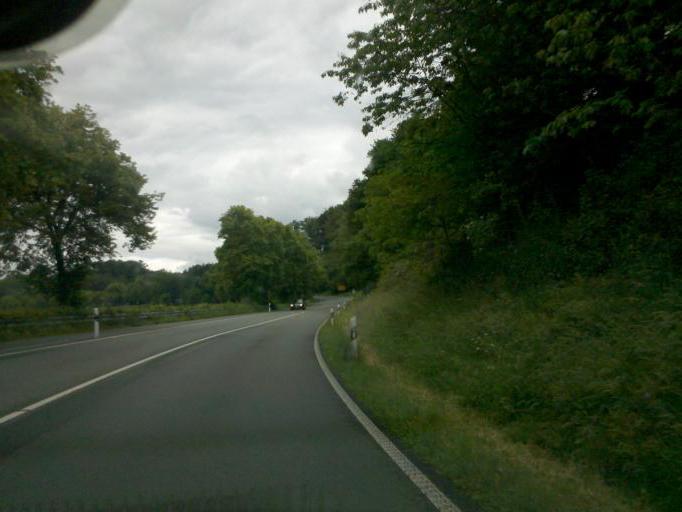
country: DE
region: North Rhine-Westphalia
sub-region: Regierungsbezirk Arnsberg
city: Meschede
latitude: 51.3050
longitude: 8.2588
